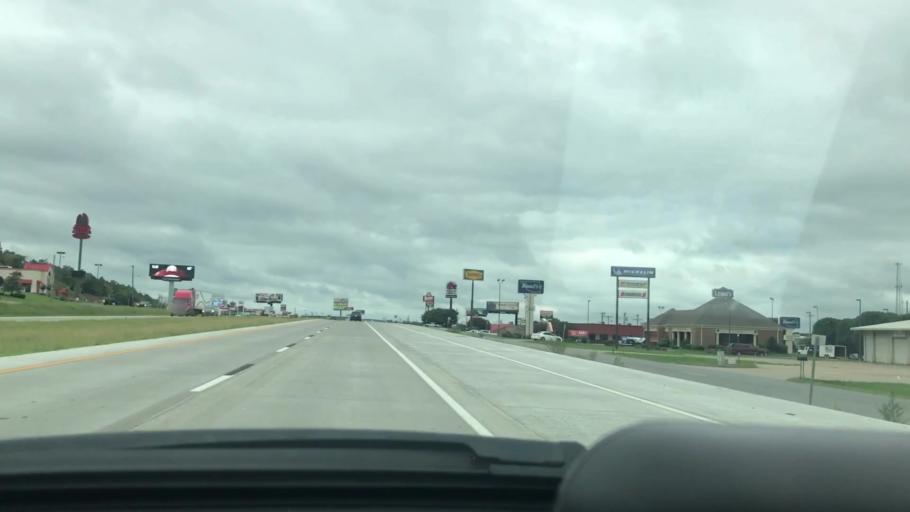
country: US
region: Oklahoma
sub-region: Pittsburg County
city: McAlester
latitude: 34.9146
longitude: -95.7452
